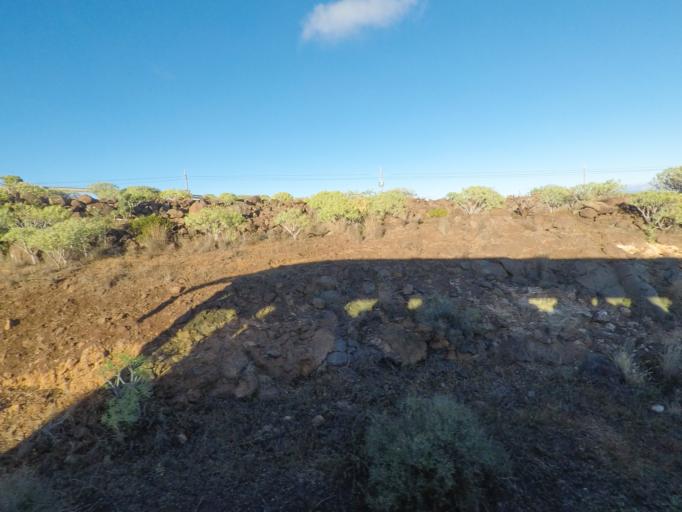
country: ES
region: Canary Islands
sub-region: Provincia de Santa Cruz de Tenerife
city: San Sebastian de la Gomera
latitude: 28.0866
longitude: -17.1458
